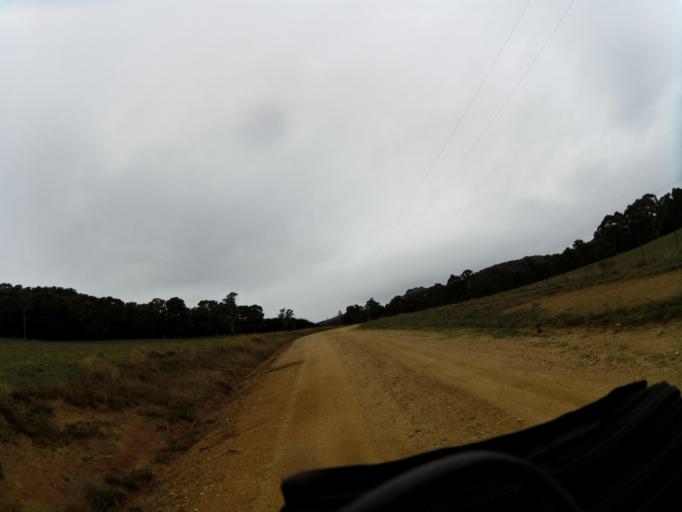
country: AU
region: New South Wales
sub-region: Greater Hume Shire
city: Holbrook
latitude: -36.1654
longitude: 147.4952
